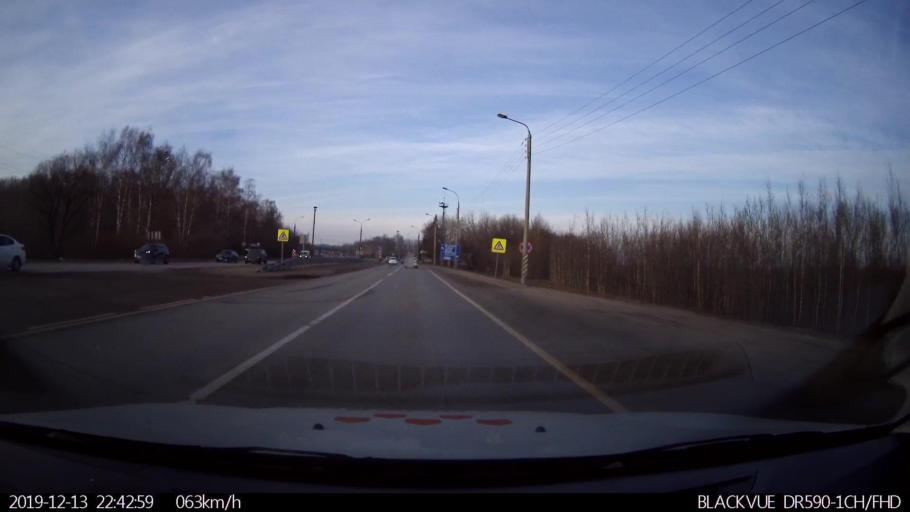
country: RU
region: Nizjnij Novgorod
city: Afonino
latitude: 56.1933
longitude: 44.1285
